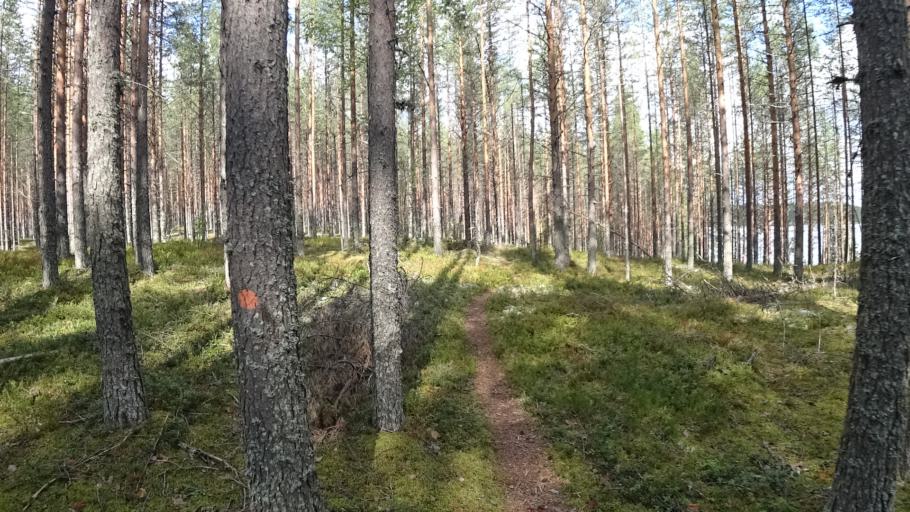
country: FI
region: North Karelia
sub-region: Joensuu
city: Ilomantsi
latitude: 62.6049
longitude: 31.1893
